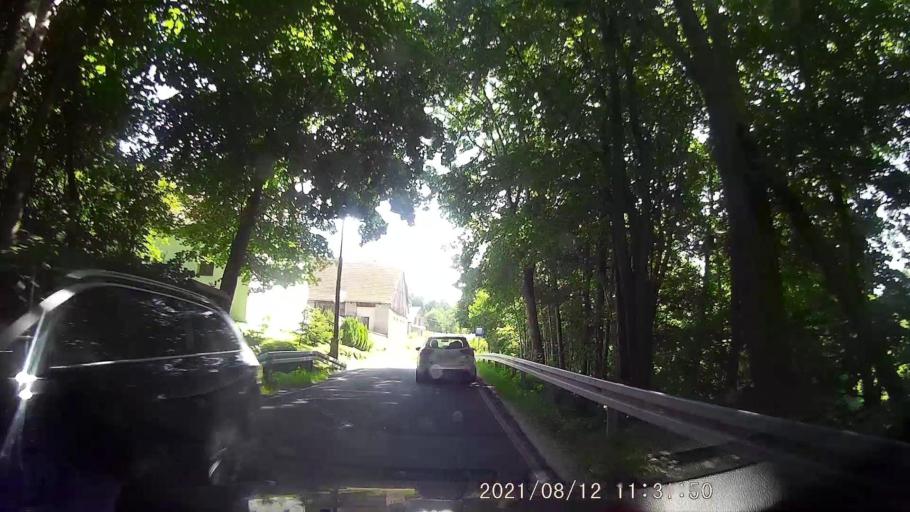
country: PL
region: Lower Silesian Voivodeship
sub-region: Powiat klodzki
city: Bystrzyca Klodzka
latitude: 50.2749
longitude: 16.7327
